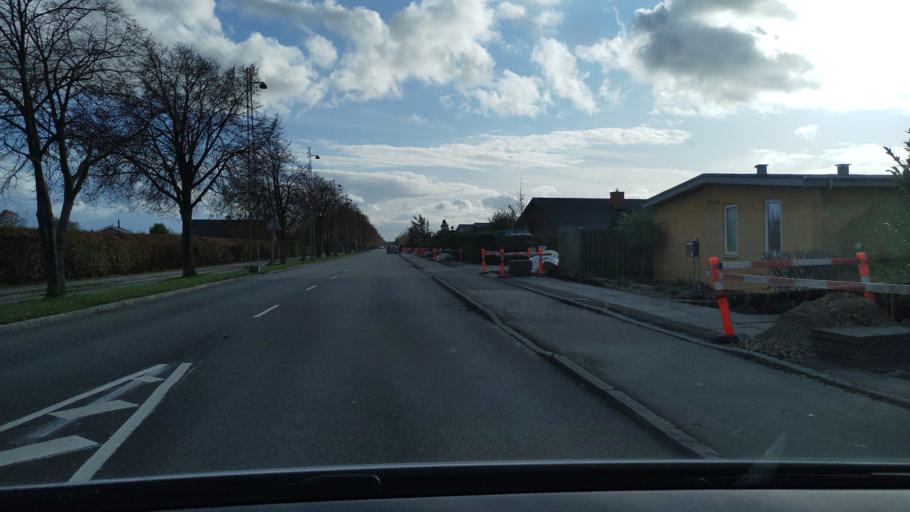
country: DK
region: Capital Region
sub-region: Tarnby Kommune
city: Tarnby
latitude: 55.6207
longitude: 12.5922
